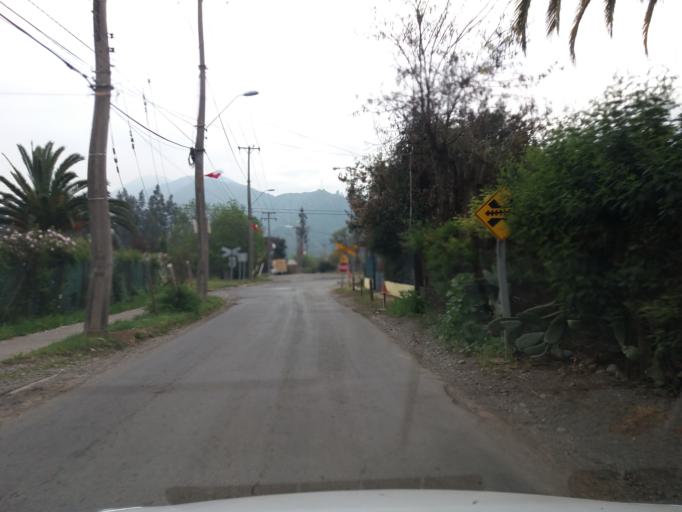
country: CL
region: Valparaiso
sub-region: Provincia de Quillota
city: Hacienda La Calera
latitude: -32.8471
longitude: -71.1036
